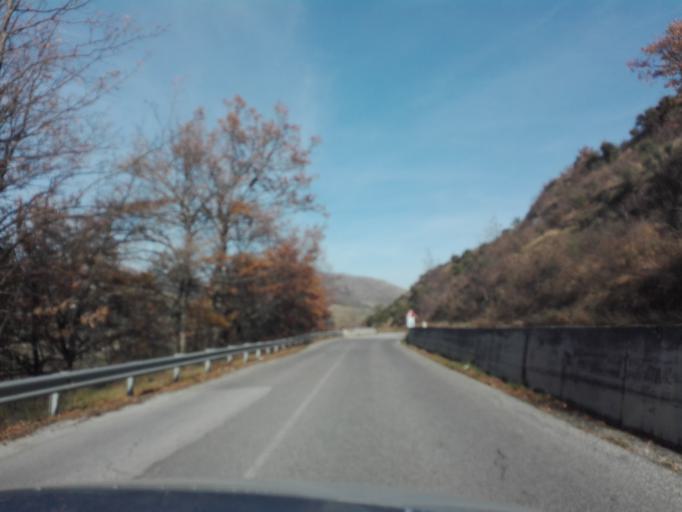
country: IT
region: Molise
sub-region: Provincia di Isernia
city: Agnone
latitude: 41.8199
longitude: 14.3731
